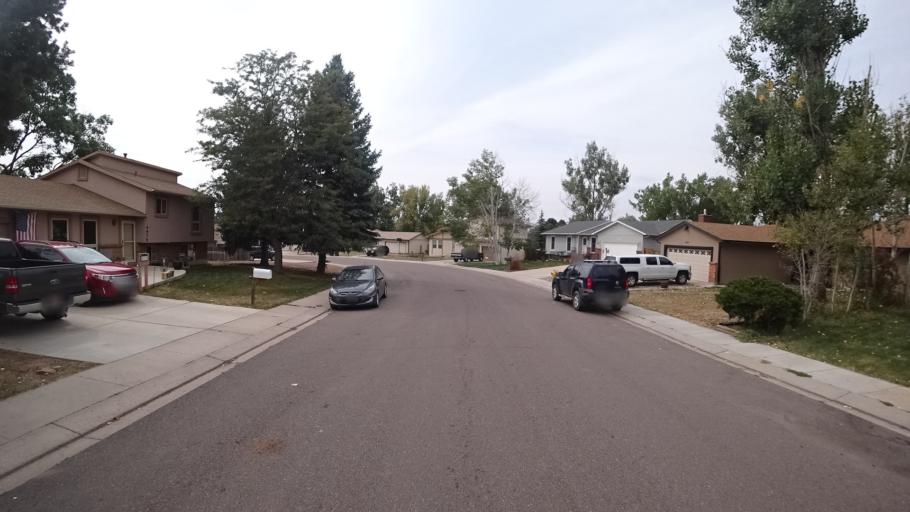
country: US
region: Colorado
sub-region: El Paso County
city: Cimarron Hills
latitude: 38.9011
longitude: -104.7349
